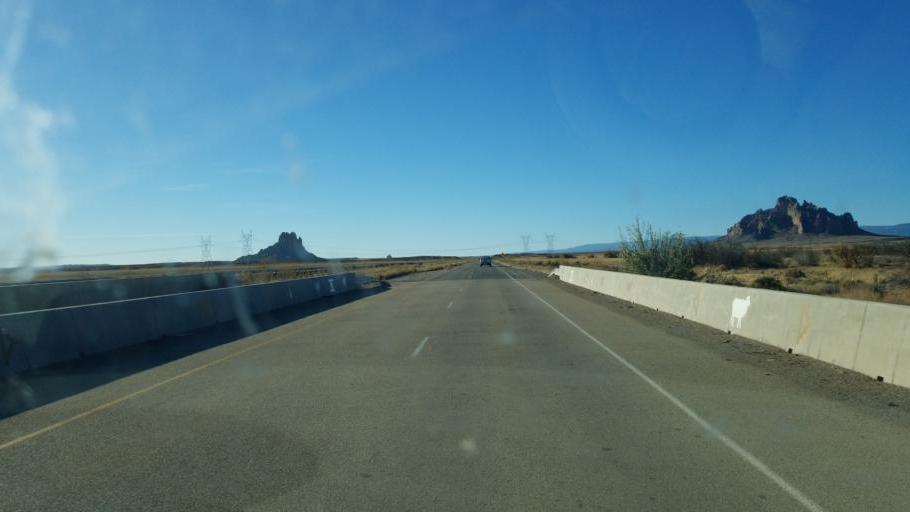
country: US
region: New Mexico
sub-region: San Juan County
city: Shiprock
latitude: 36.4180
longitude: -108.7214
